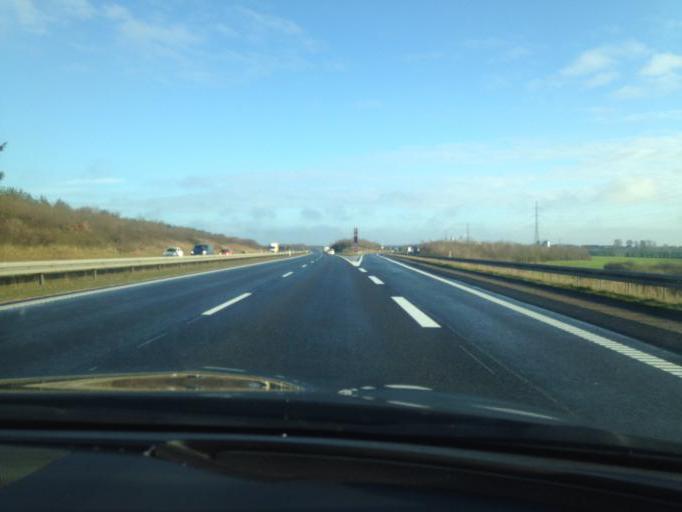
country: DK
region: South Denmark
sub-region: Kolding Kommune
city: Kolding
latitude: 55.5115
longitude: 9.3860
